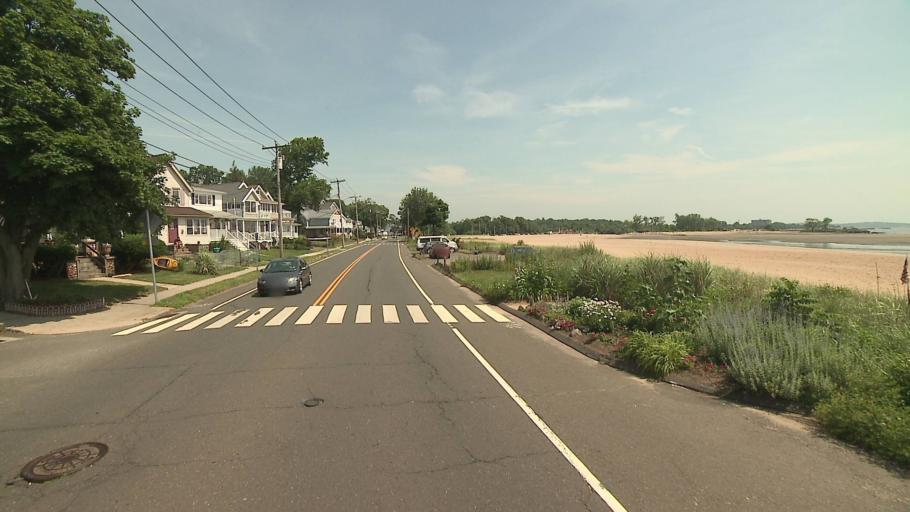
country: US
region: Connecticut
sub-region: New Haven County
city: West Haven
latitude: 41.2493
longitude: -72.9634
